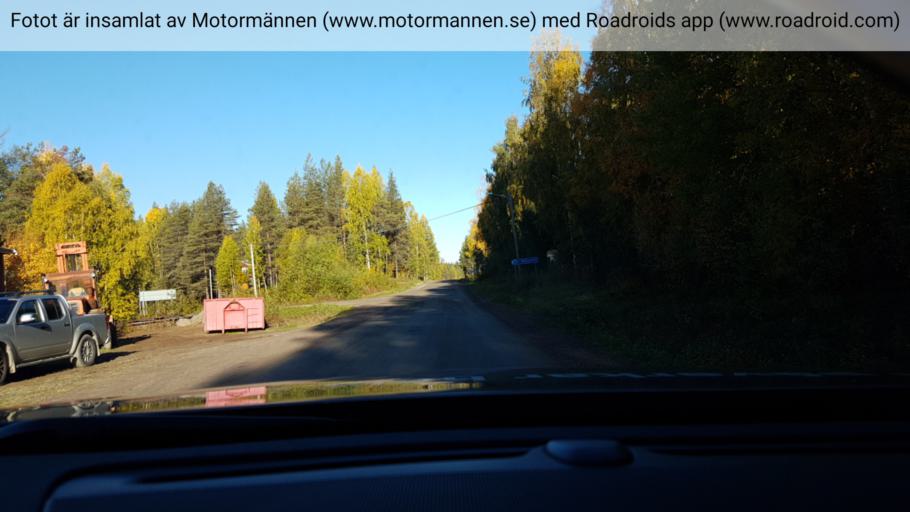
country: SE
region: Norrbotten
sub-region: Alvsbyns Kommun
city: AElvsbyn
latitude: 66.1962
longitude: 21.1881
